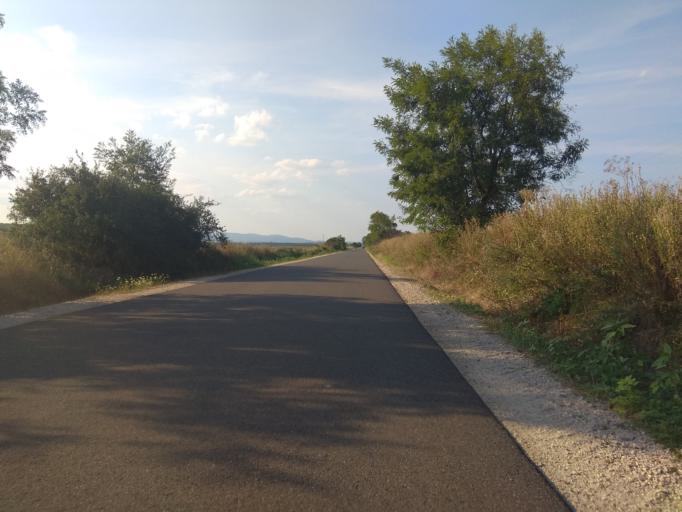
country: HU
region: Borsod-Abauj-Zemplen
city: Harsany
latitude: 47.9027
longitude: 20.7446
